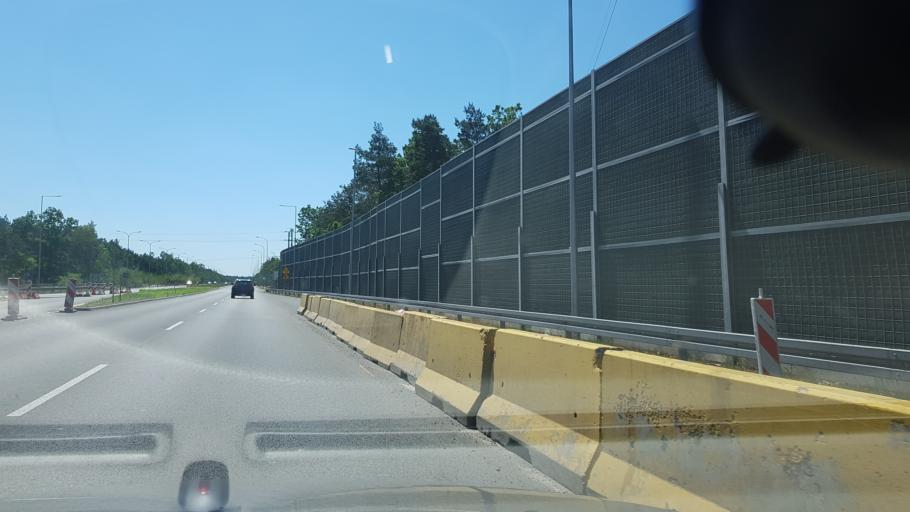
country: PL
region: Masovian Voivodeship
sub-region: Warszawa
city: Rembertow
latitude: 52.2801
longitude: 21.1413
